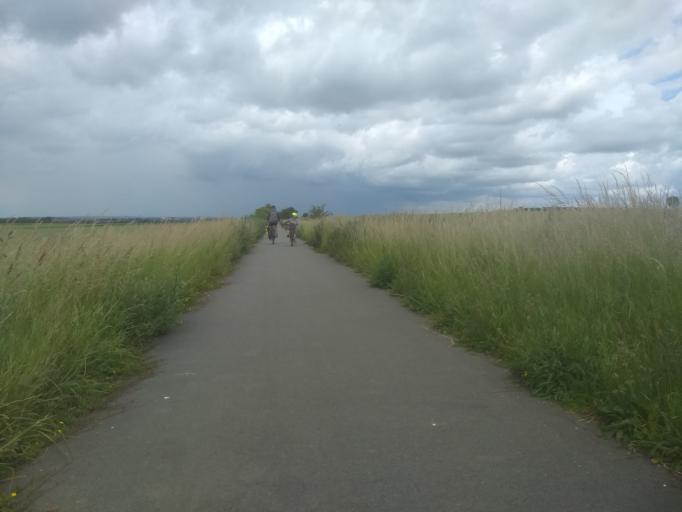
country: FR
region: Nord-Pas-de-Calais
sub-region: Departement du Pas-de-Calais
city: Riviere
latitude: 50.2540
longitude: 2.6990
